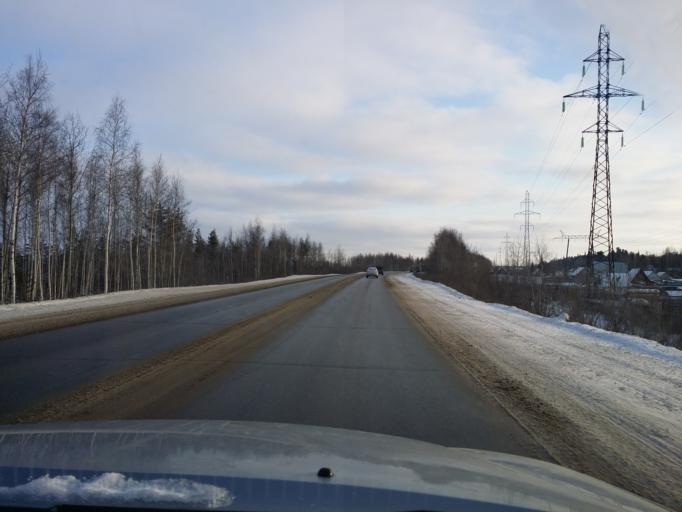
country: RU
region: Khanty-Mansiyskiy Avtonomnyy Okrug
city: Nizhnevartovsk
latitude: 61.0443
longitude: 76.3489
